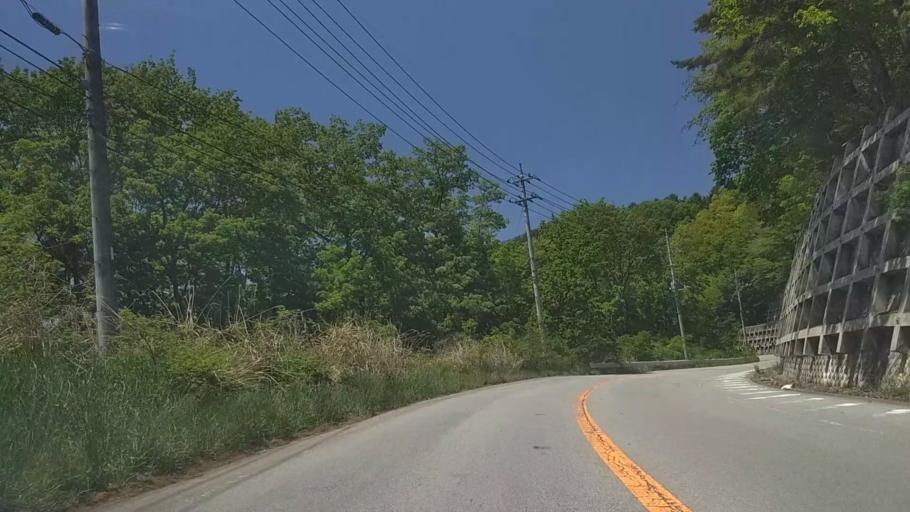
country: JP
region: Yamanashi
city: Nirasaki
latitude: 35.8779
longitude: 138.4377
